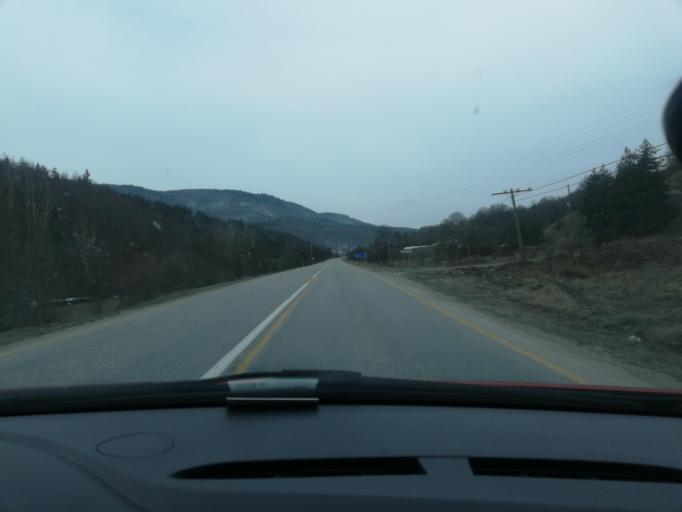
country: TR
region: Kastamonu
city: Kure
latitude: 41.7529
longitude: 33.6997
